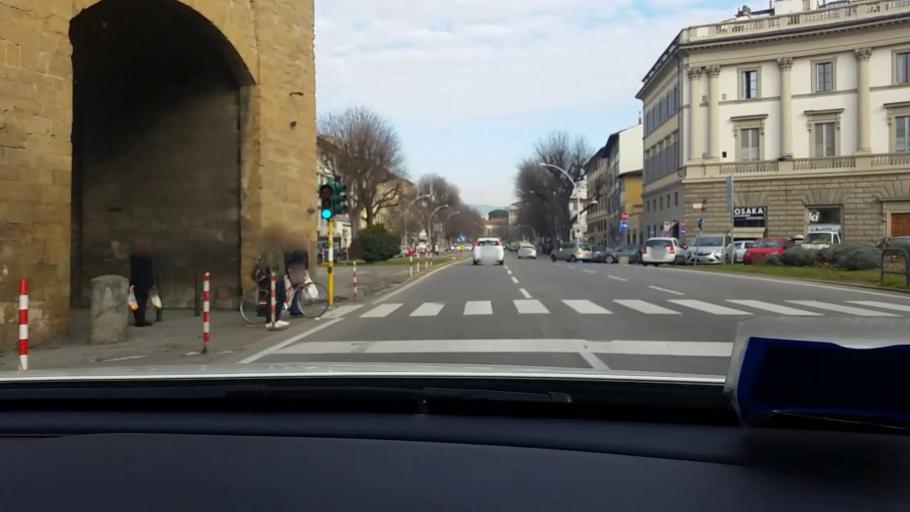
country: IT
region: Tuscany
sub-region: Province of Florence
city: Florence
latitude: 43.7705
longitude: 11.2710
